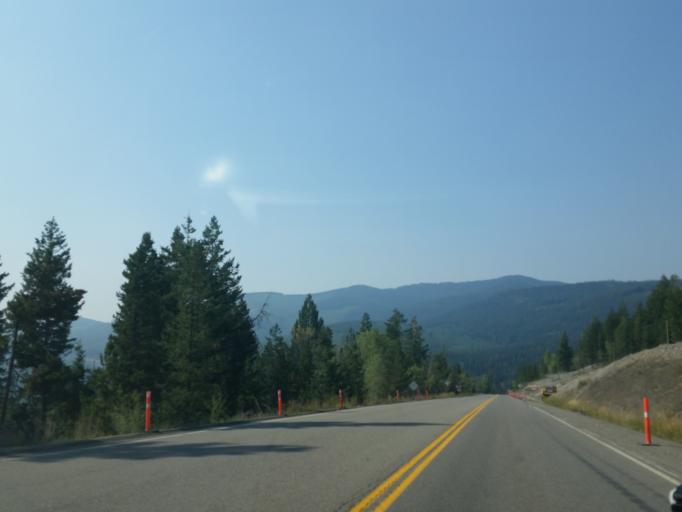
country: CA
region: British Columbia
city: Princeton
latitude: 49.2744
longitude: -120.5757
